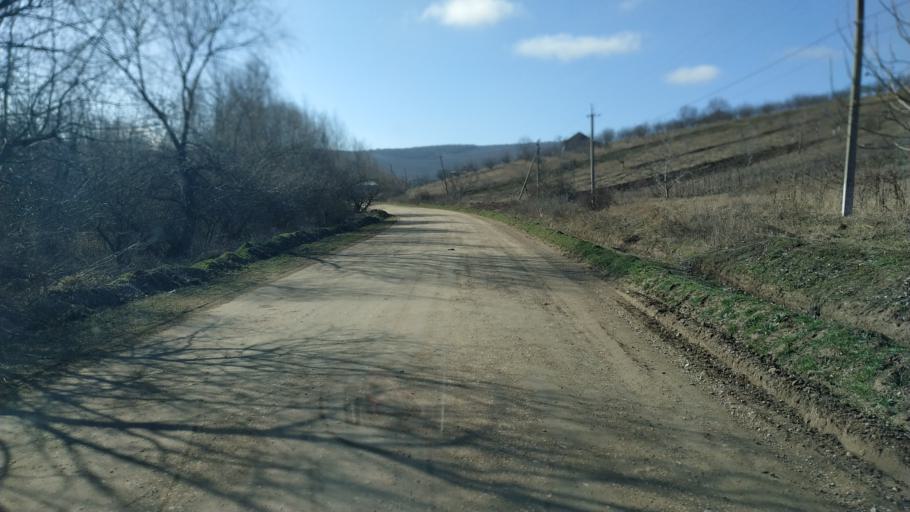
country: MD
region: Hincesti
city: Hincesti
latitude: 46.9269
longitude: 28.6294
